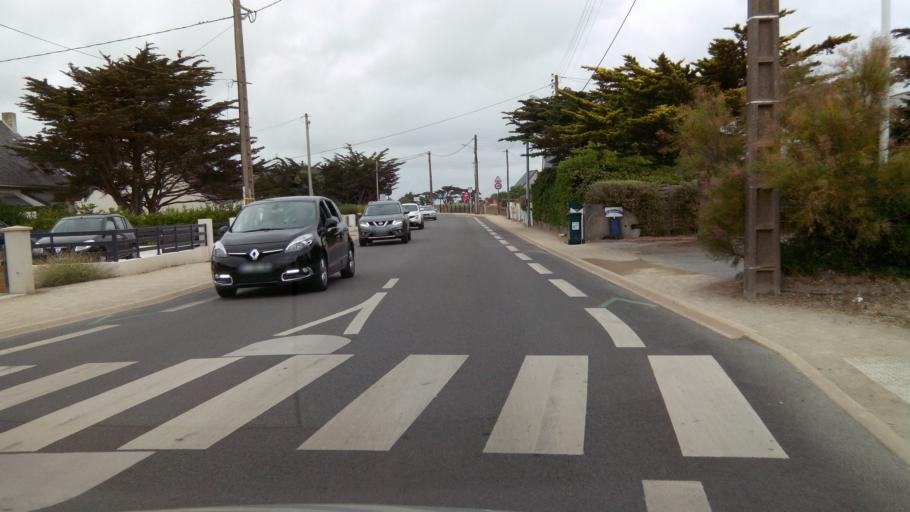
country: FR
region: Pays de la Loire
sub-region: Departement de la Loire-Atlantique
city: Batz-sur-Mer
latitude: 47.2772
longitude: -2.4925
